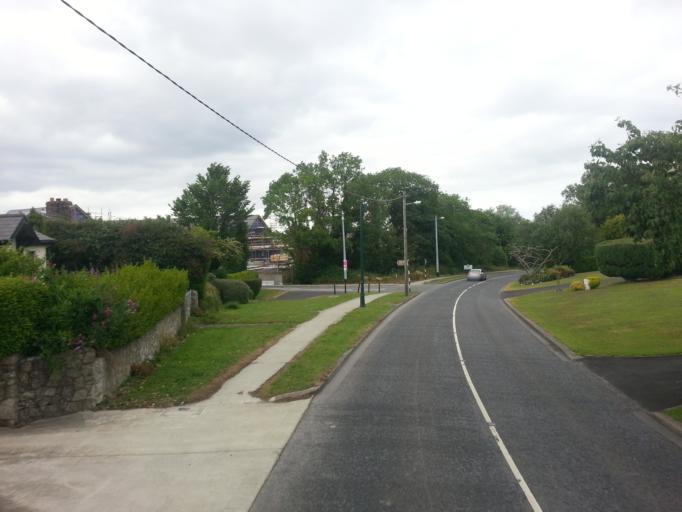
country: IE
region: Leinster
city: Sandyford
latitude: 53.2561
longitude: -6.2157
